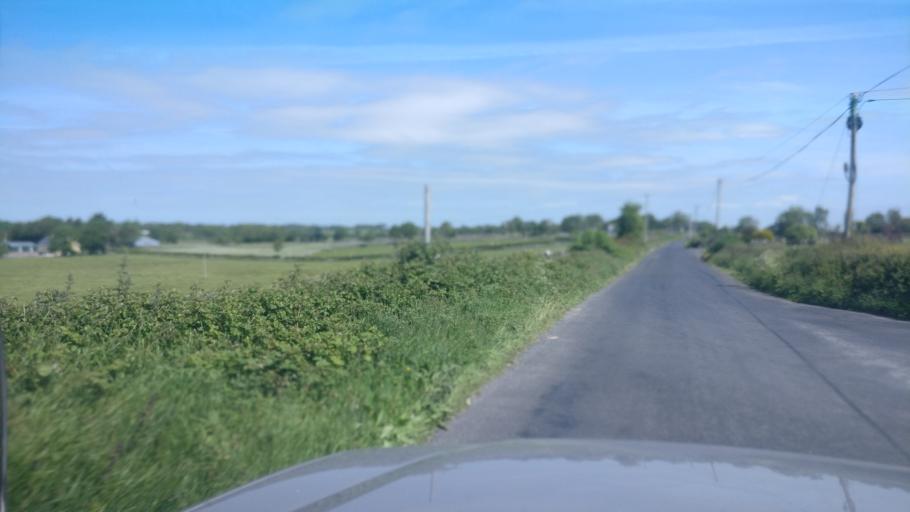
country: IE
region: Connaught
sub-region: County Galway
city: Gort
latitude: 53.1352
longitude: -8.7701
